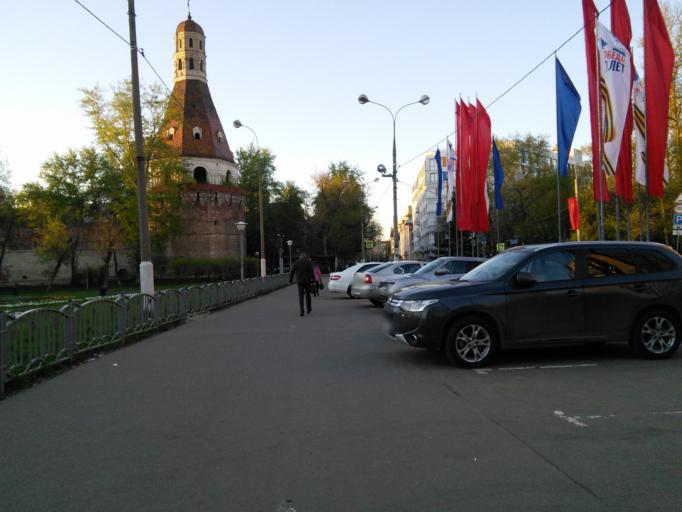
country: RU
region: Moskovskaya
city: Kozhukhovo
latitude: 55.7127
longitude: 37.6583
